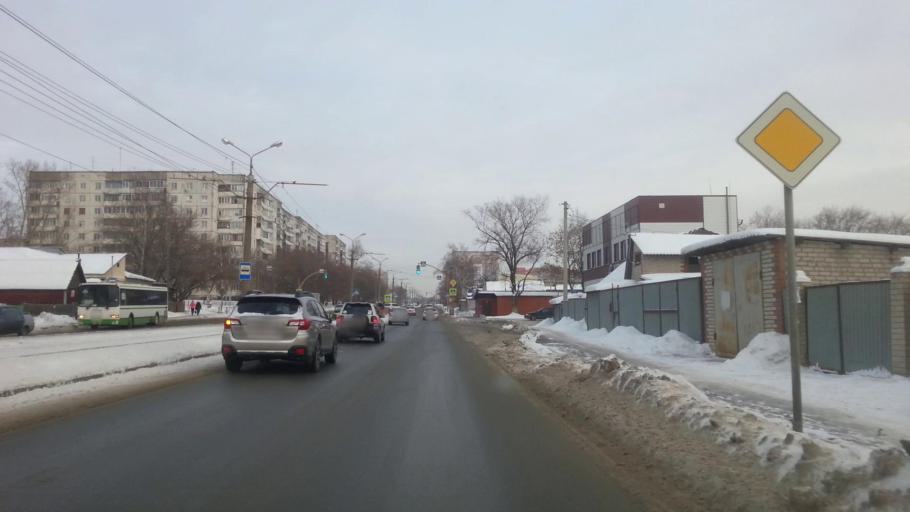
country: RU
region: Altai Krai
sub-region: Gorod Barnaulskiy
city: Barnaul
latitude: 53.3683
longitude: 83.7371
